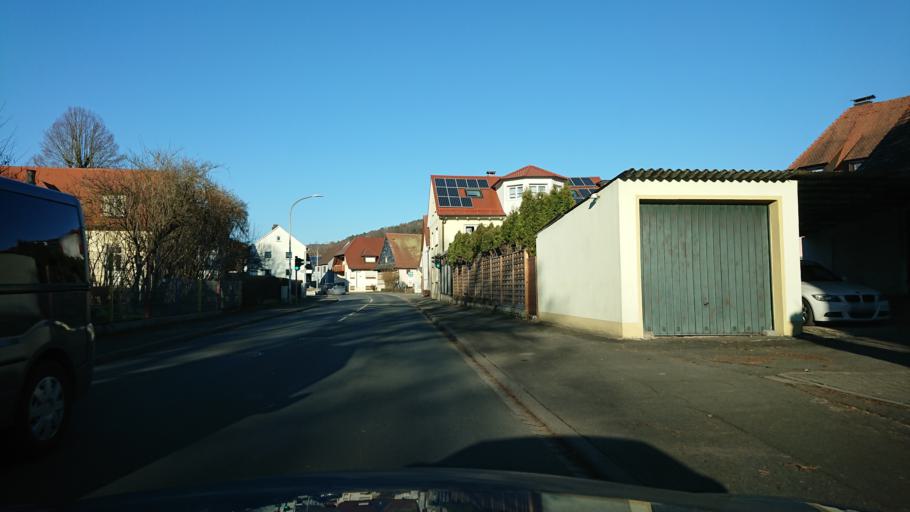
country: DE
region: Bavaria
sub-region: Upper Franconia
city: Pretzfeld
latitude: 49.7536
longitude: 11.1722
